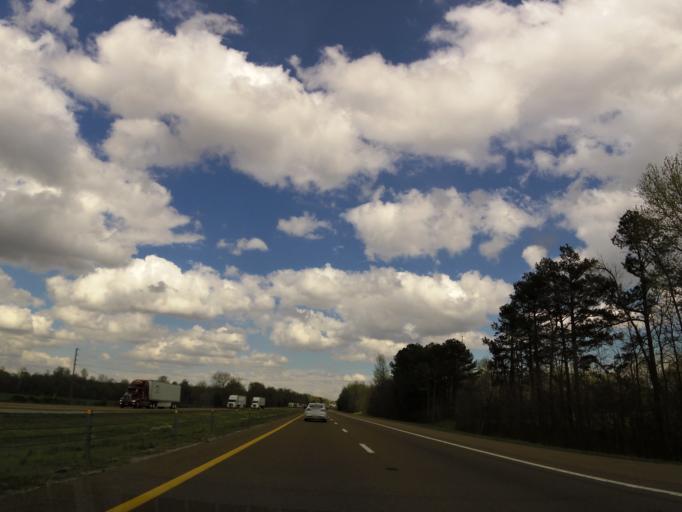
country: US
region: Tennessee
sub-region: Crockett County
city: Bells
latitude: 35.6085
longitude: -89.0253
